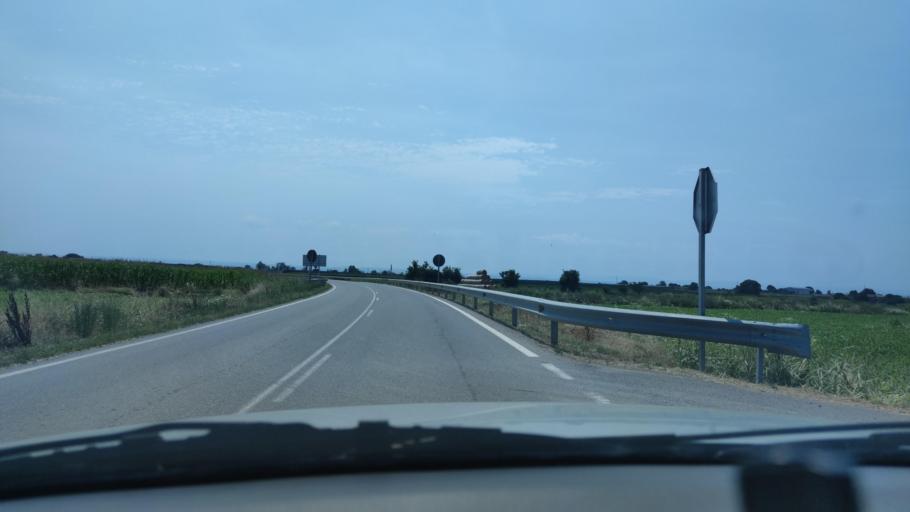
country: ES
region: Catalonia
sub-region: Provincia de Lleida
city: Ivars d'Urgell
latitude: 41.6791
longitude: 0.9797
